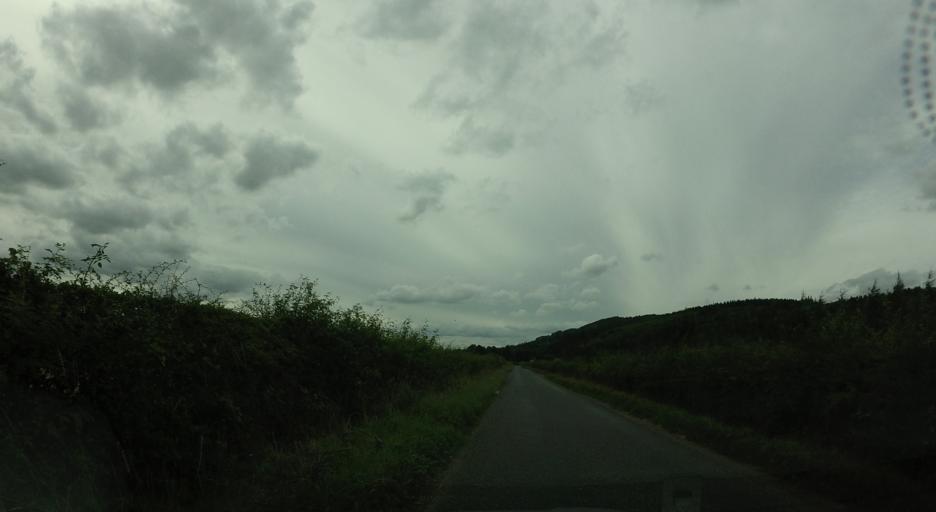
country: GB
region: Scotland
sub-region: Perth and Kinross
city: Bridge of Earn
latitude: 56.3534
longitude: -3.3584
